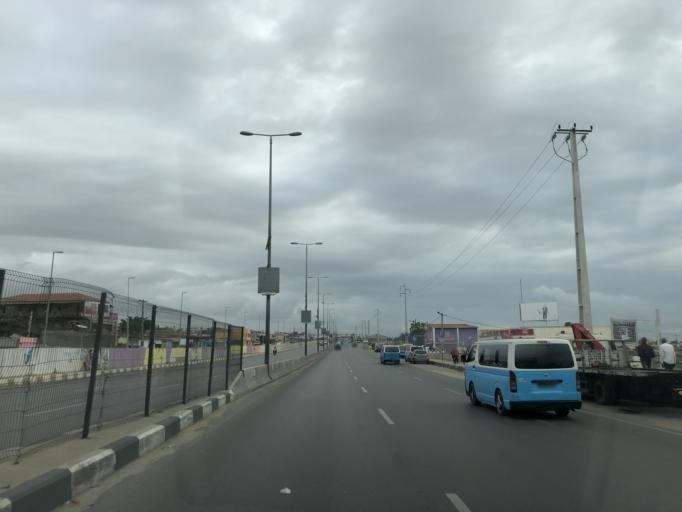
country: AO
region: Luanda
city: Luanda
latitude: -8.8564
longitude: 13.2181
